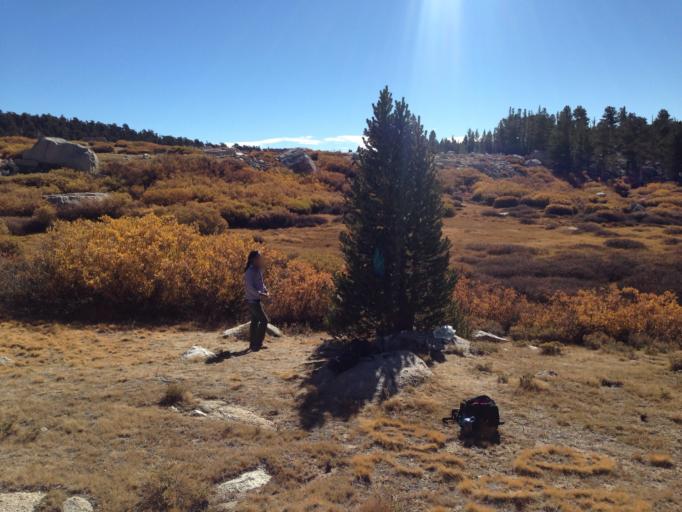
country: US
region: California
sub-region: Inyo County
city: Lone Pine
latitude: 36.5000
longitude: -118.2212
